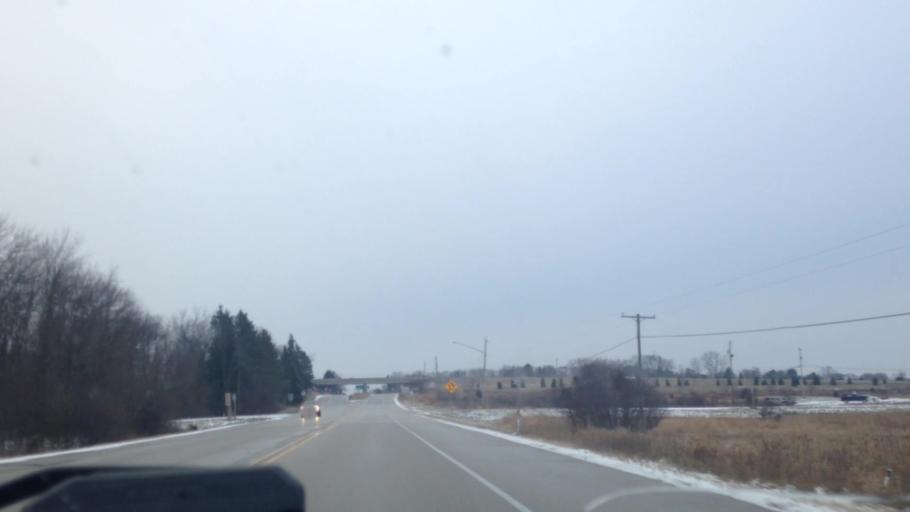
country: US
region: Wisconsin
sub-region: Waukesha County
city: Oconomowoc
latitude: 43.1531
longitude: -88.4997
